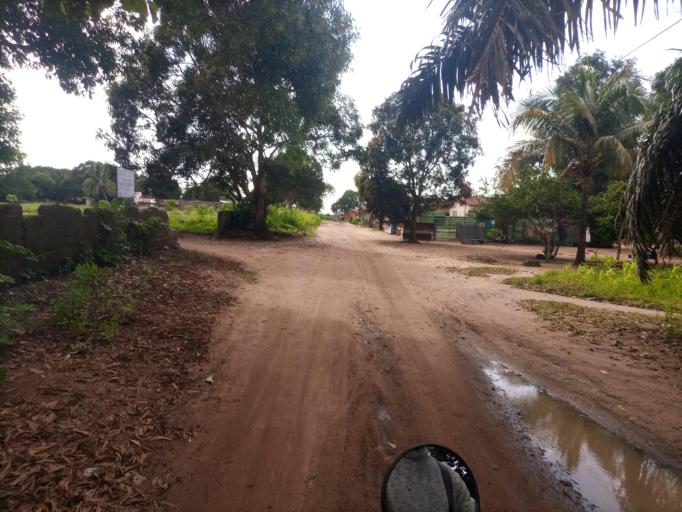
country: SL
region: Northern Province
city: Masoyila
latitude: 8.6095
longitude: -13.1809
